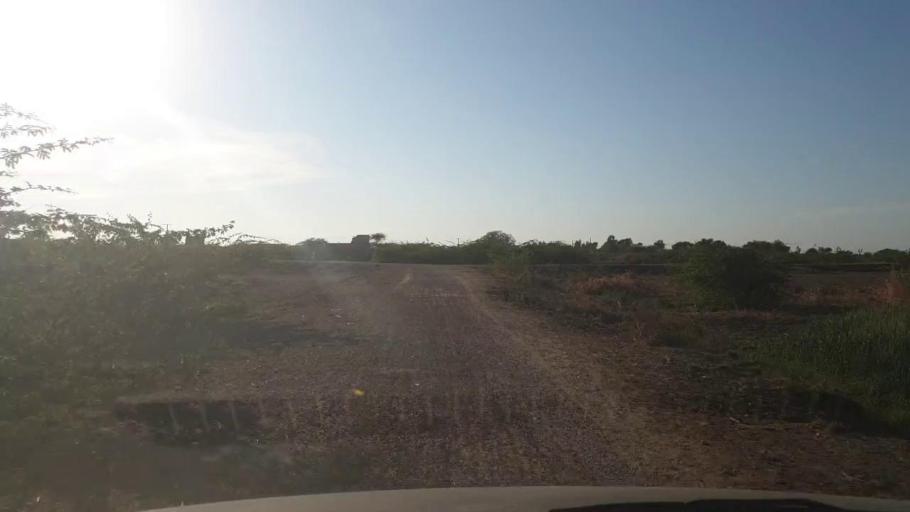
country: PK
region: Sindh
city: Dhoro Naro
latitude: 25.4088
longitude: 69.5578
